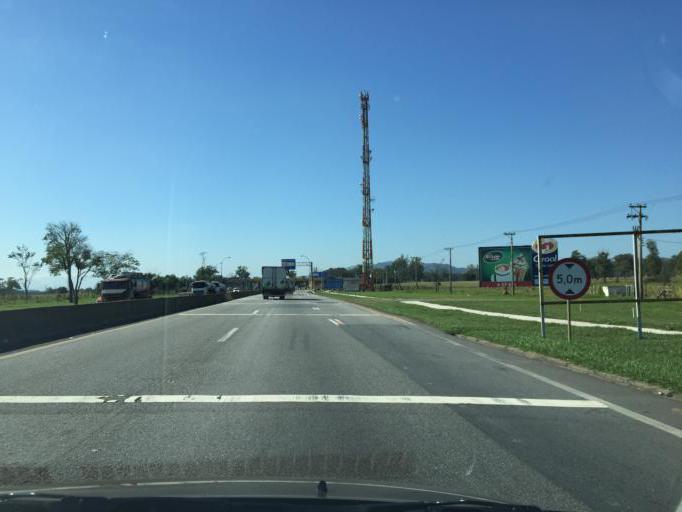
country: BR
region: Sao Paulo
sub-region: Pindamonhangaba
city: Pindamonhangaba
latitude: -22.9320
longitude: -45.3643
